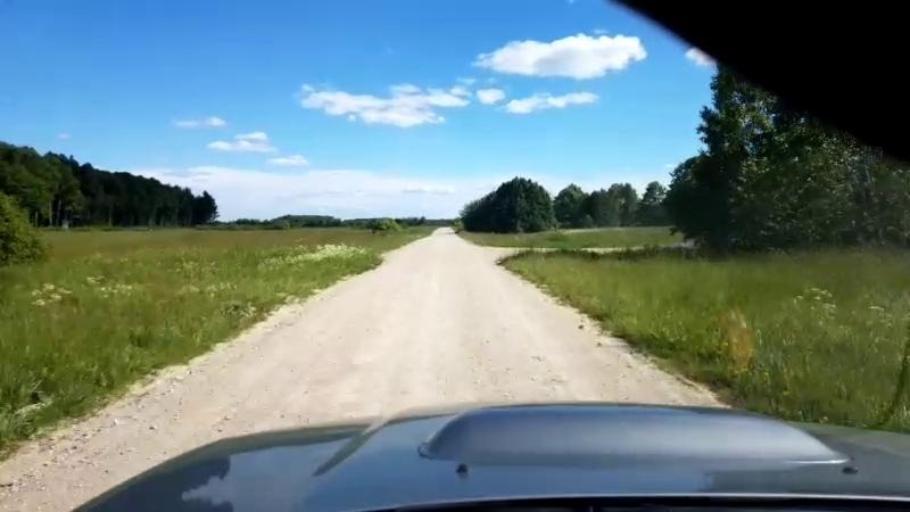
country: EE
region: Paernumaa
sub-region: Sauga vald
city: Sauga
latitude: 58.5063
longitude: 24.5201
